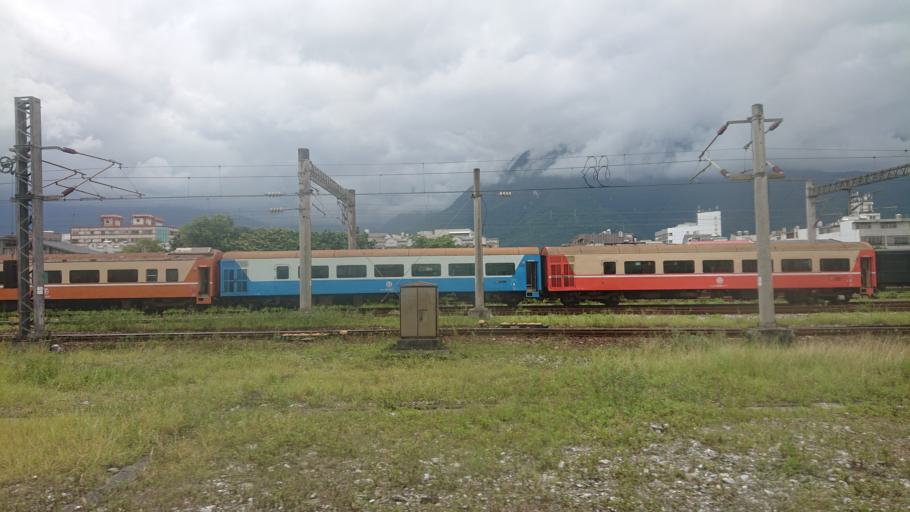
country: TW
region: Taiwan
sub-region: Hualien
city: Hualian
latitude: 23.9965
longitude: 121.6027
